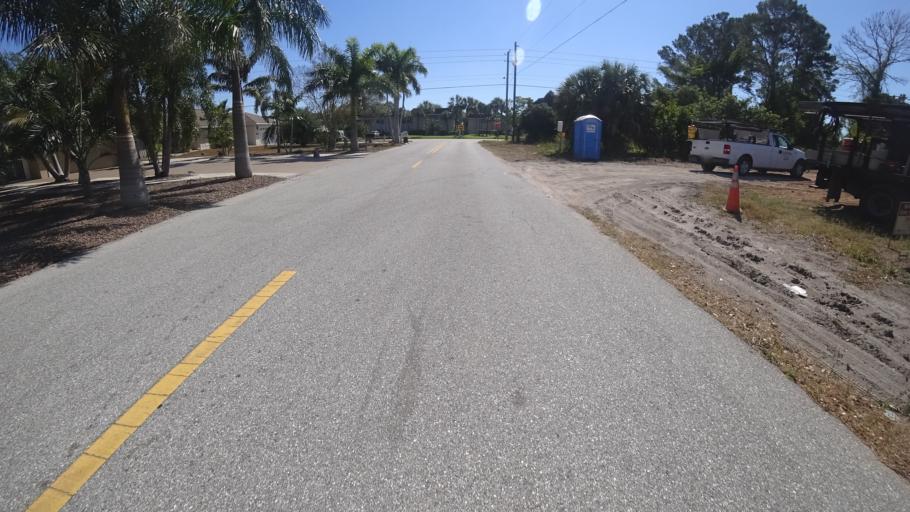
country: US
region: Florida
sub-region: Manatee County
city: West Bradenton
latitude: 27.4772
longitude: -82.6376
